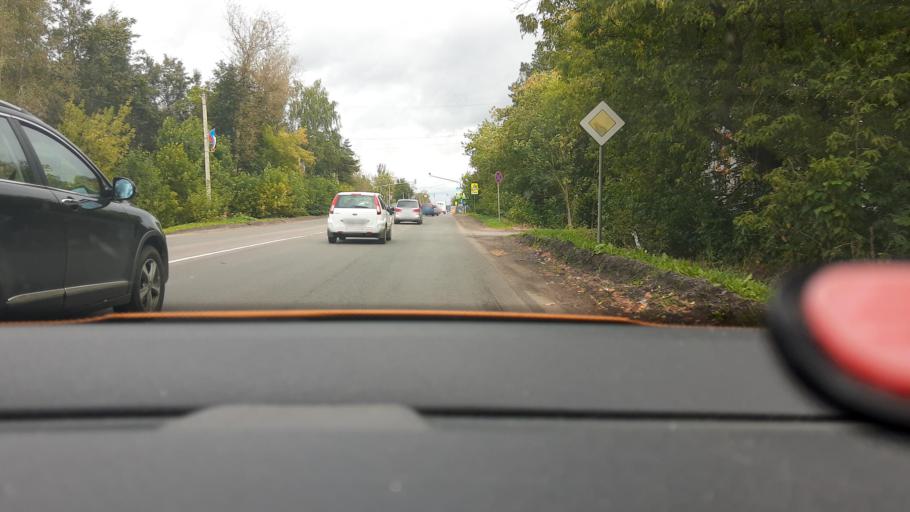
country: RU
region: Moskovskaya
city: Kostino
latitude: 56.0435
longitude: 37.9772
